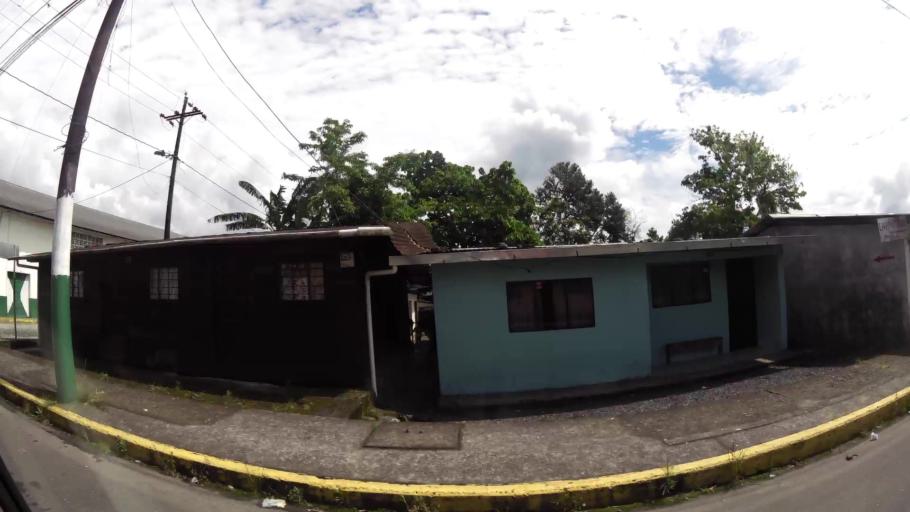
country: EC
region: Pastaza
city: Puyo
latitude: -1.4612
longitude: -78.1125
